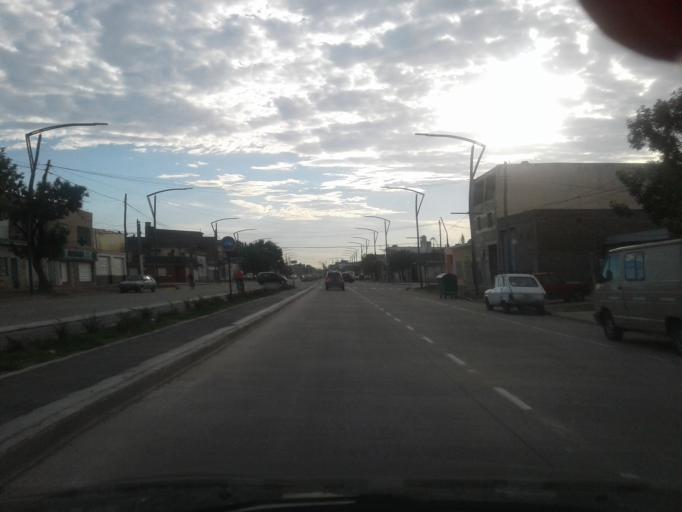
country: AR
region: Santa Fe
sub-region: Departamento de Rosario
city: Rosario
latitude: -32.9592
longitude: -60.7047
